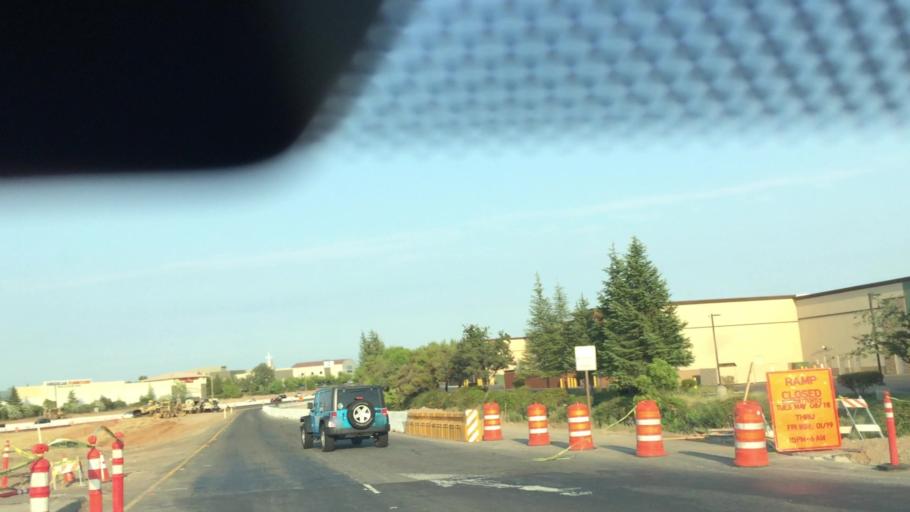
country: US
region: California
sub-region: Placer County
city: Roseville
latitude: 38.7756
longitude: -121.2656
